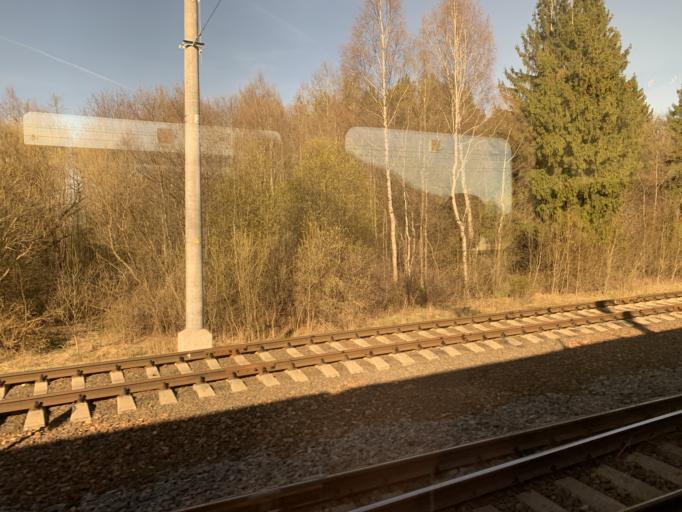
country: BY
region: Grodnenskaya
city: Astravyets
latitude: 54.5886
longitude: 25.9112
